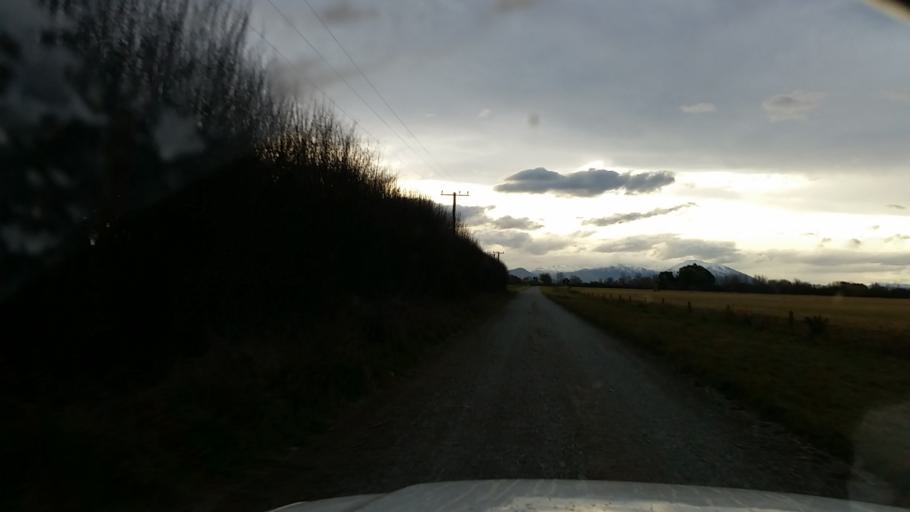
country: NZ
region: Canterbury
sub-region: Ashburton District
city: Ashburton
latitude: -43.8457
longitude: 171.6606
